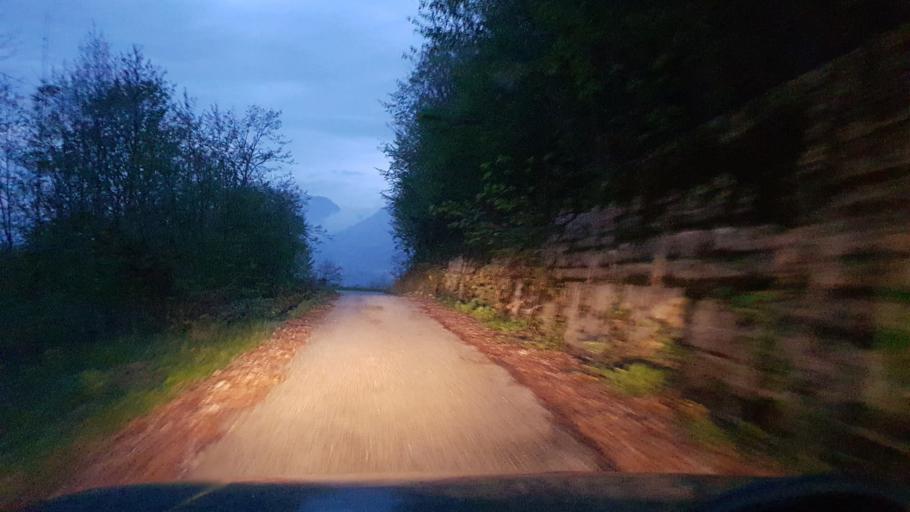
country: IT
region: Friuli Venezia Giulia
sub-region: Provincia di Udine
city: Taipana
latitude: 46.2432
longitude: 13.3561
